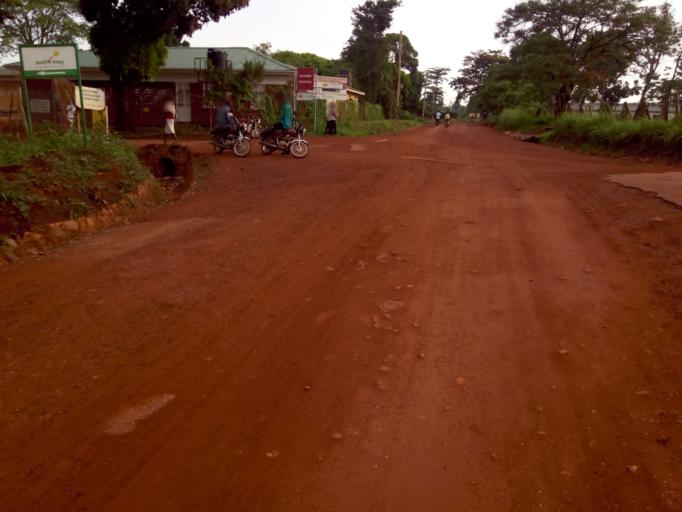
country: UG
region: Western Region
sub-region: Masindi District
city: Masindi
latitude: 1.6840
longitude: 31.7169
